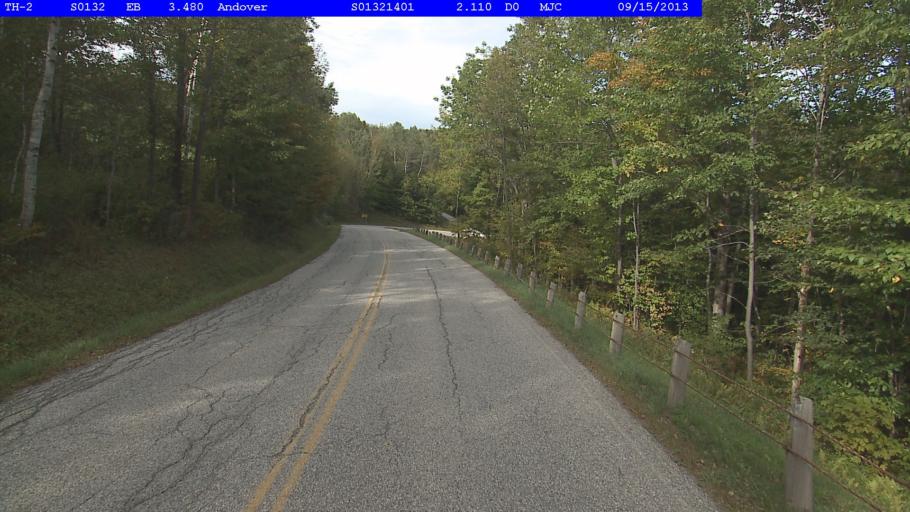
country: US
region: Vermont
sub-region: Windsor County
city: Chester
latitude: 43.2863
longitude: -72.7264
